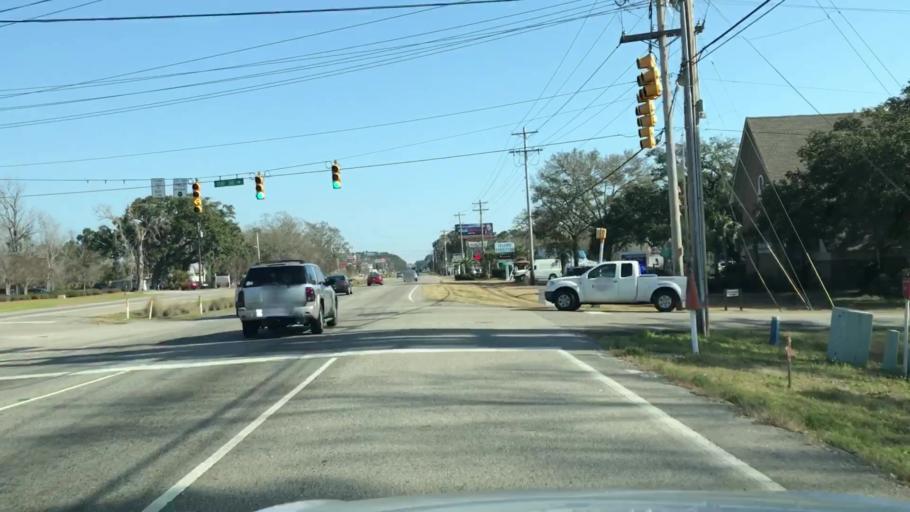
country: US
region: South Carolina
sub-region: Horry County
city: Garden City
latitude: 33.5889
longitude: -79.0079
